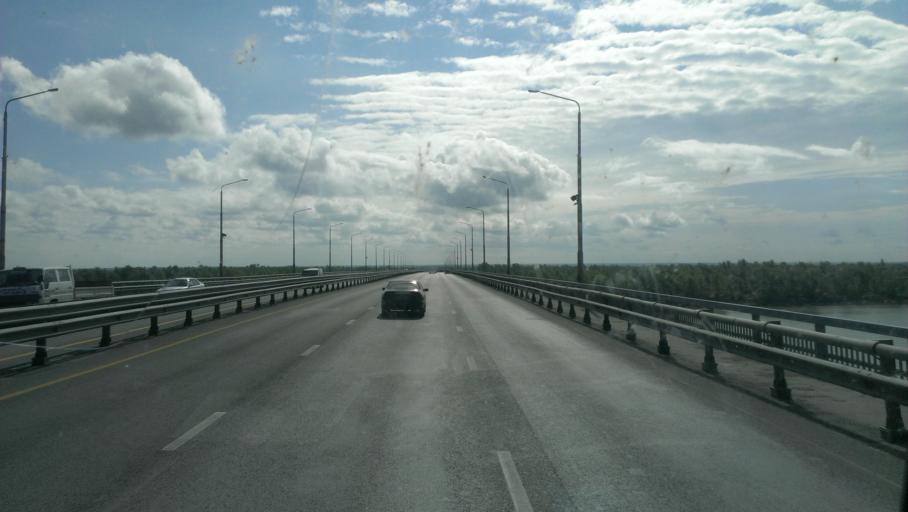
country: RU
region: Altai Krai
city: Zaton
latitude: 53.3241
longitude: 83.8010
